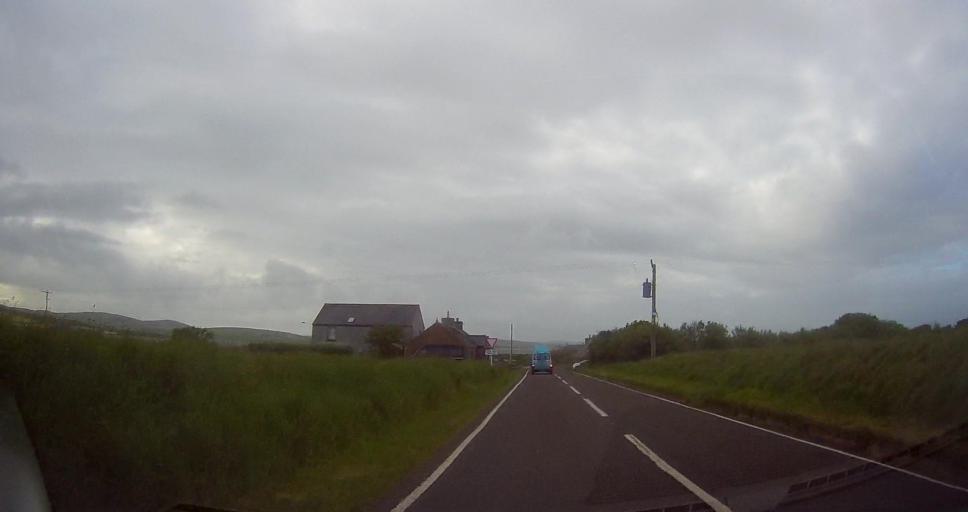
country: GB
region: Scotland
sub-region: Orkney Islands
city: Stromness
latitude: 58.9822
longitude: -3.2465
